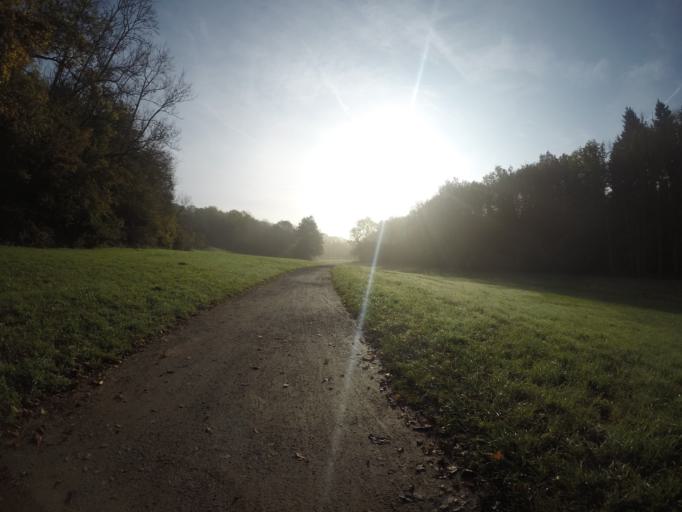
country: DE
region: Baden-Wuerttemberg
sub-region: Regierungsbezirk Stuttgart
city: Leinfelden-Echterdingen
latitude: 48.7138
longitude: 9.1768
